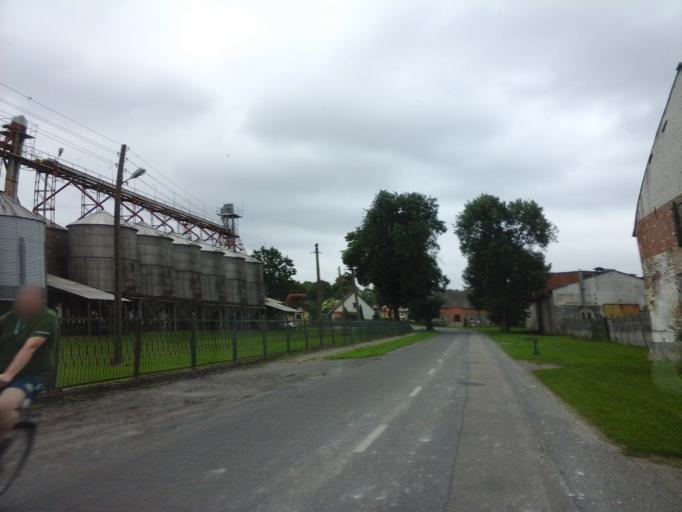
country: PL
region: West Pomeranian Voivodeship
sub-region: Powiat choszczenski
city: Pelczyce
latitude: 53.1161
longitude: 15.2525
